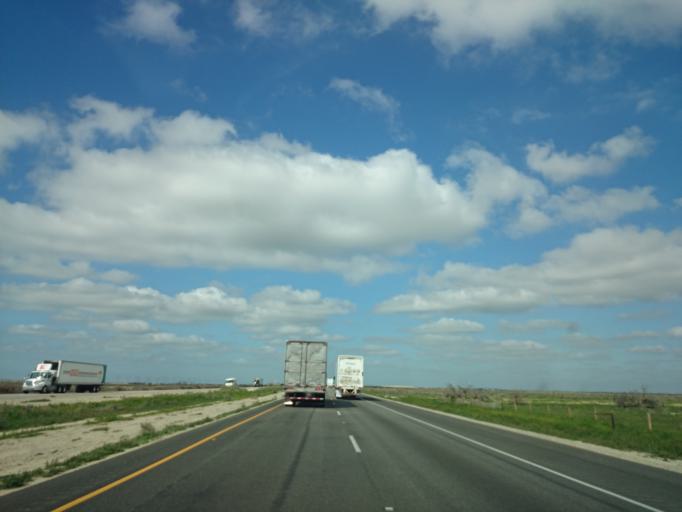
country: US
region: California
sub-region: Kern County
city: Rosedale
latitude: 35.2534
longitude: -119.2098
